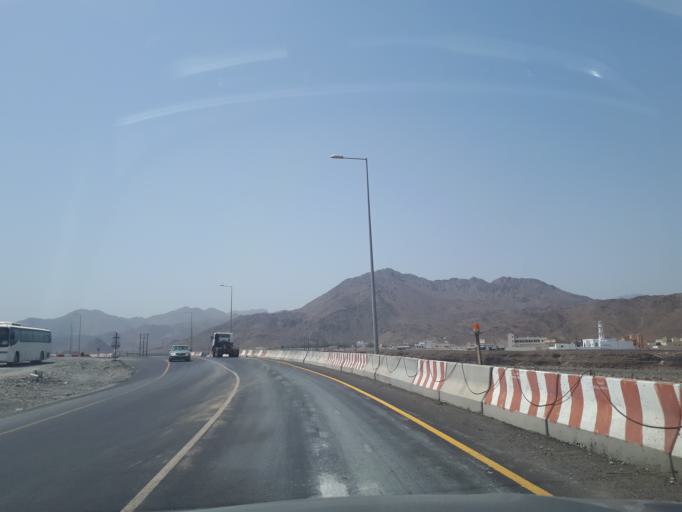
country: OM
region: Muhafazat ad Dakhiliyah
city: Sufalat Sama'il
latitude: 23.2648
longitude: 58.1035
